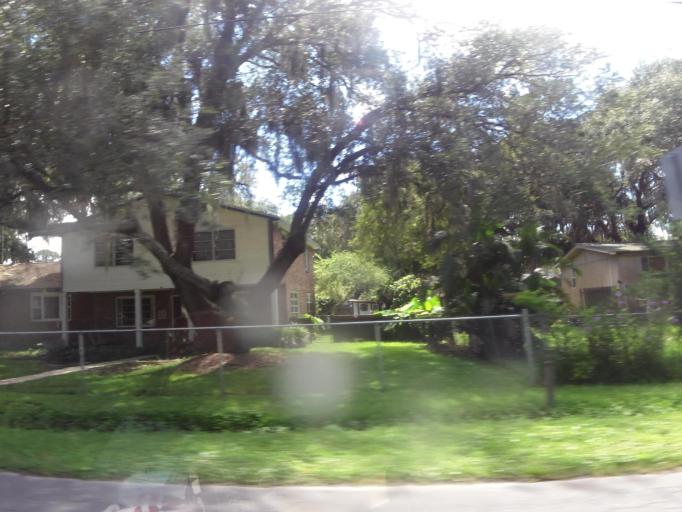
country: US
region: Florida
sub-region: Nassau County
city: Fernandina Beach
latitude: 30.6362
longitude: -81.4625
